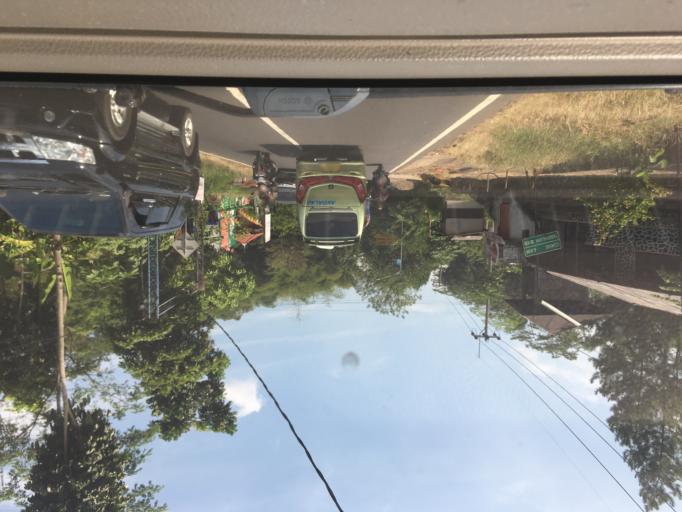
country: ID
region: West Java
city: Tagog
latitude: -7.1174
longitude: 108.1317
